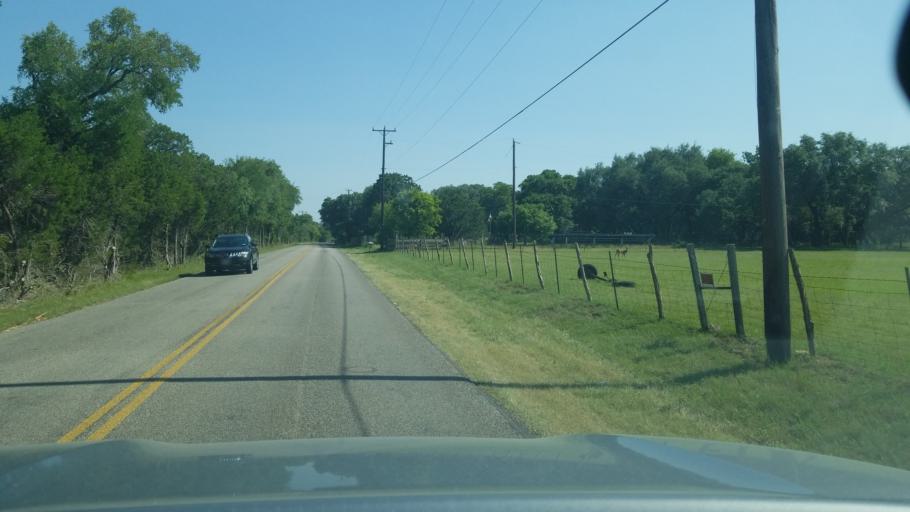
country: US
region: Texas
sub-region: Bexar County
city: Timberwood Park
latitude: 29.7471
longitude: -98.5128
